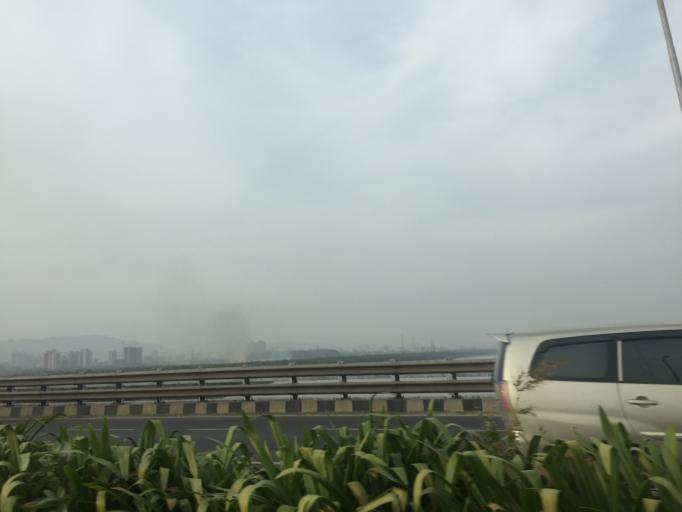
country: IN
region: Maharashtra
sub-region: Thane
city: Airoli
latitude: 19.1508
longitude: 72.9804
